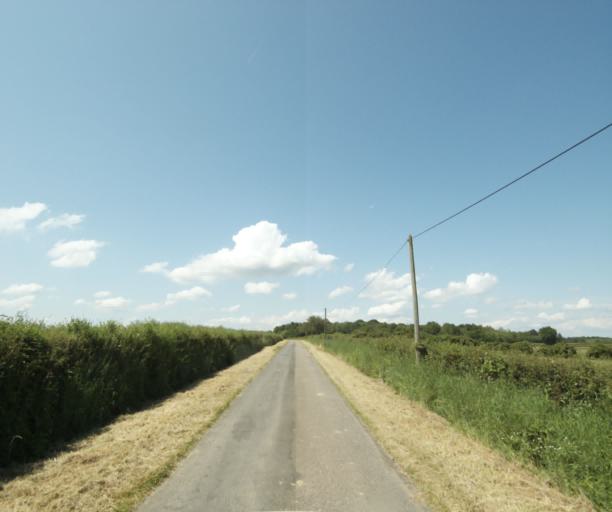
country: FR
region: Bourgogne
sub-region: Departement de Saone-et-Loire
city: Perrecy-les-Forges
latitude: 46.5851
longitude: 4.1613
